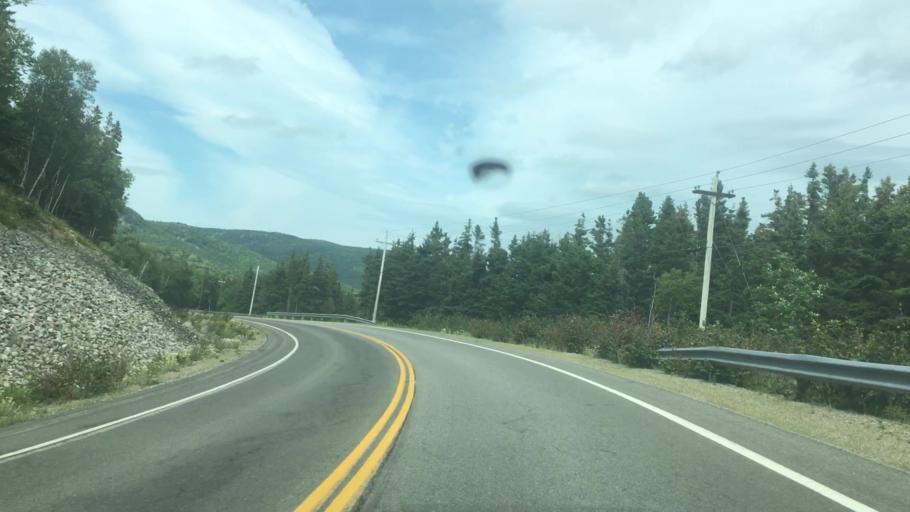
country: CA
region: Nova Scotia
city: Sydney Mines
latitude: 46.5371
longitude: -60.4134
